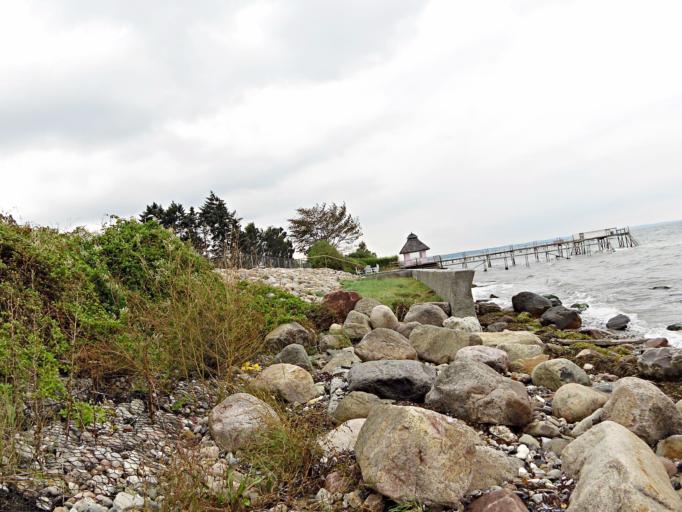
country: DK
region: Capital Region
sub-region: Horsholm Kommune
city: Horsholm
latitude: 55.8935
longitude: 12.5379
